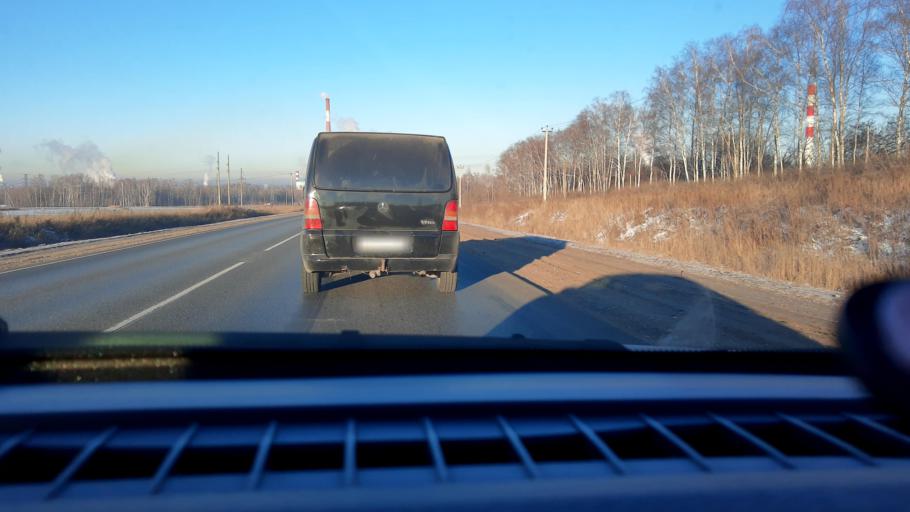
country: RU
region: Nizjnij Novgorod
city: Kstovo
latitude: 56.0915
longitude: 44.1346
